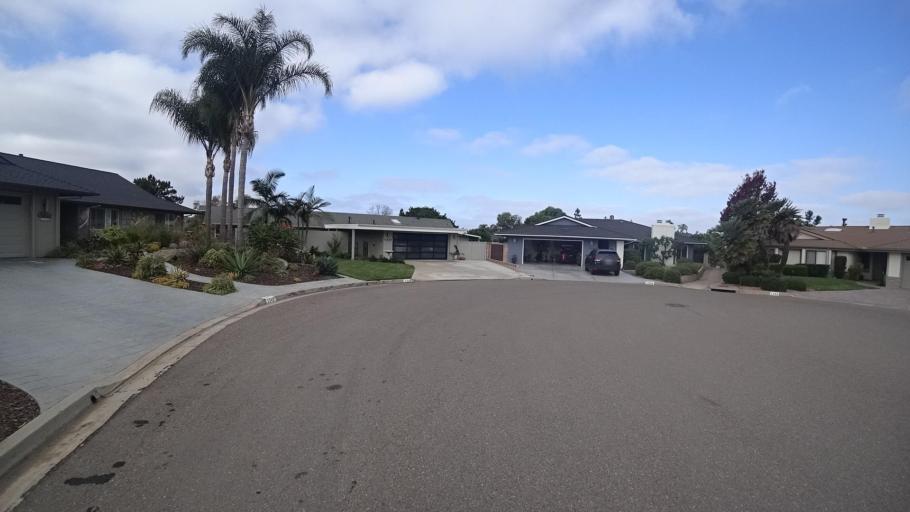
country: US
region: California
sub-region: San Diego County
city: Lake San Marcos
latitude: 33.1236
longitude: -117.2016
